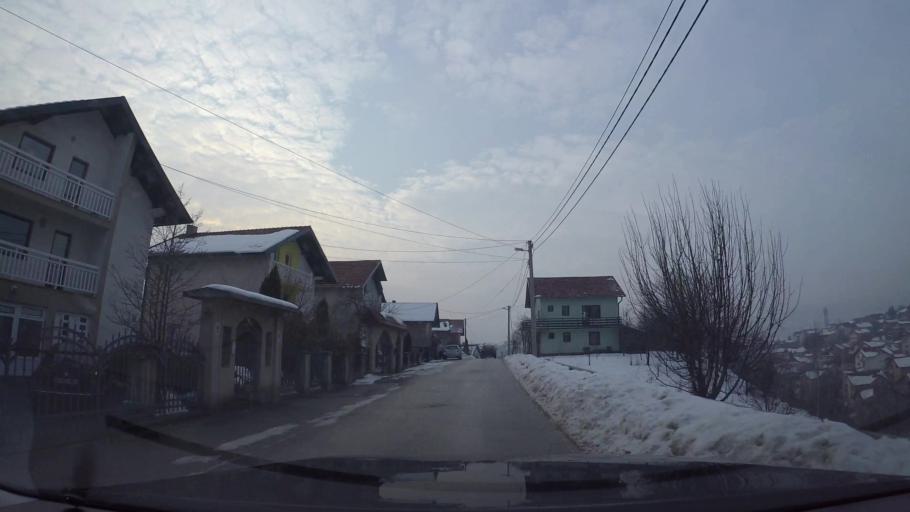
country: BA
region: Federation of Bosnia and Herzegovina
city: Hotonj
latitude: 43.8955
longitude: 18.3767
